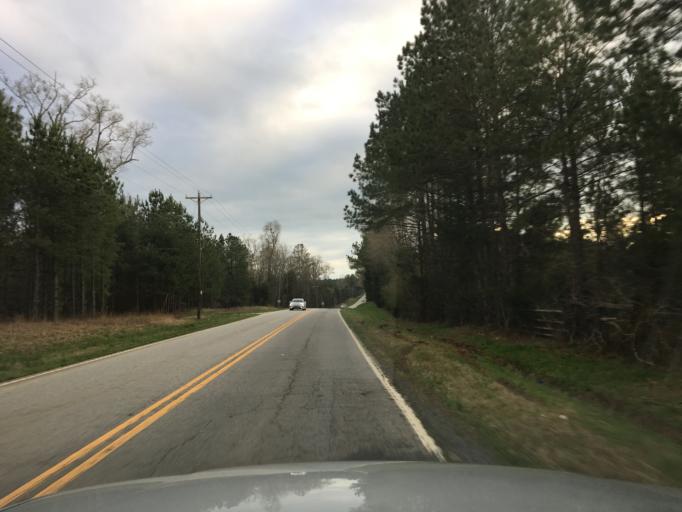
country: US
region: South Carolina
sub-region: Saluda County
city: Saluda
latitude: 33.9797
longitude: -81.7714
